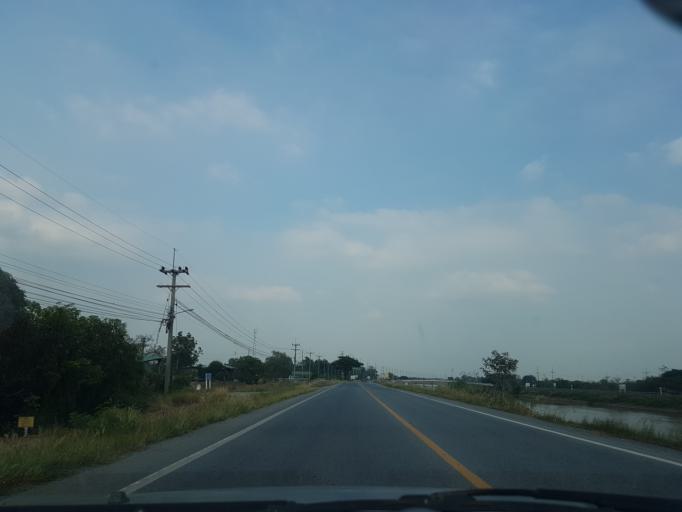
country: TH
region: Phra Nakhon Si Ayutthaya
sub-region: Amphoe Tha Ruea
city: Tha Ruea
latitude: 14.5281
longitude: 100.7426
